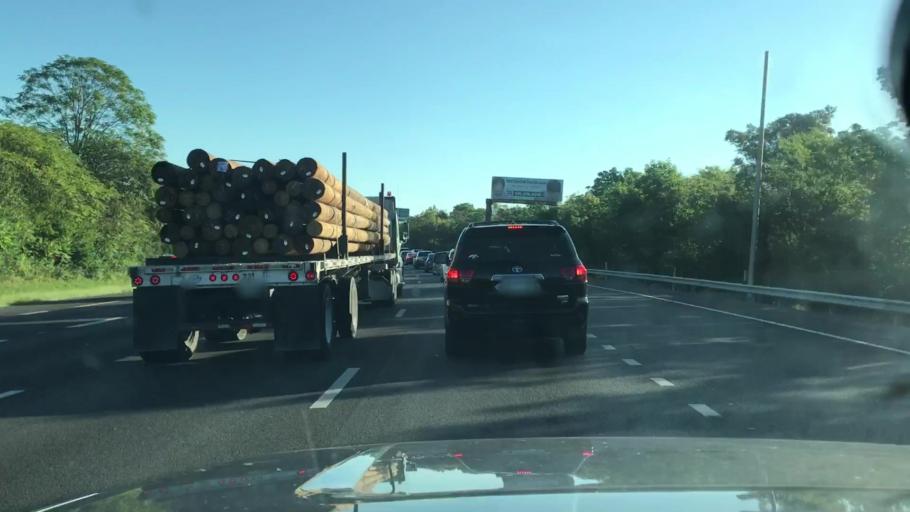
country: US
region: Tennessee
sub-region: Williamson County
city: Brentwood
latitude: 36.0448
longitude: -86.7781
